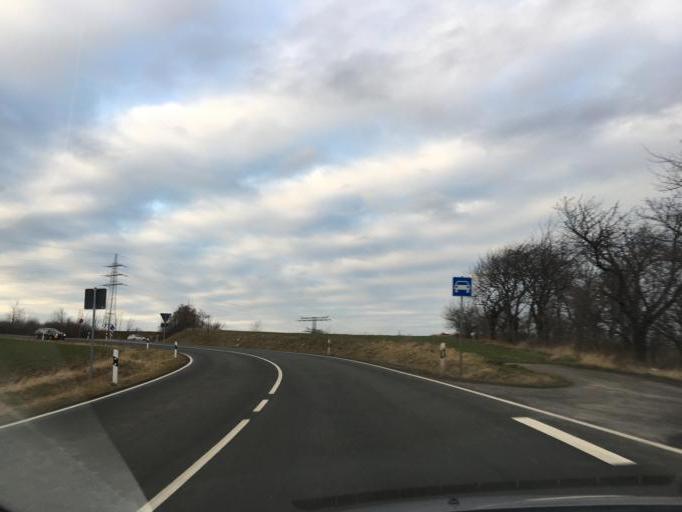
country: DE
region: Thuringia
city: Nobitz
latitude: 50.9851
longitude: 12.4676
